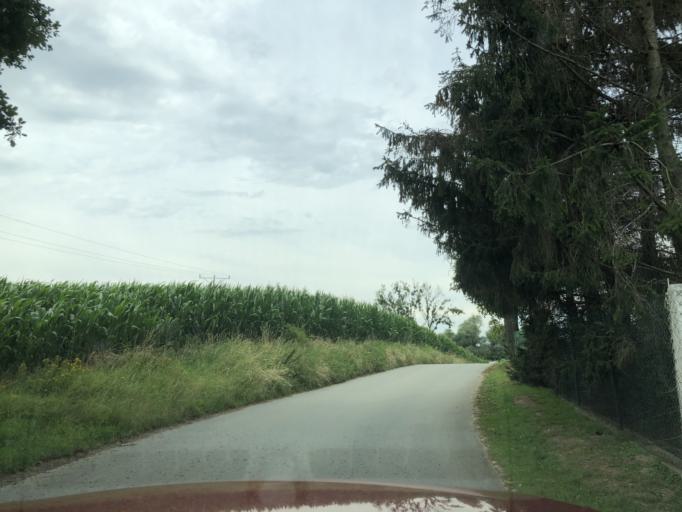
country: PL
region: Lower Silesian Voivodeship
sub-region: Powiat trzebnicki
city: Trzebnica
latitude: 51.3197
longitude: 17.0009
